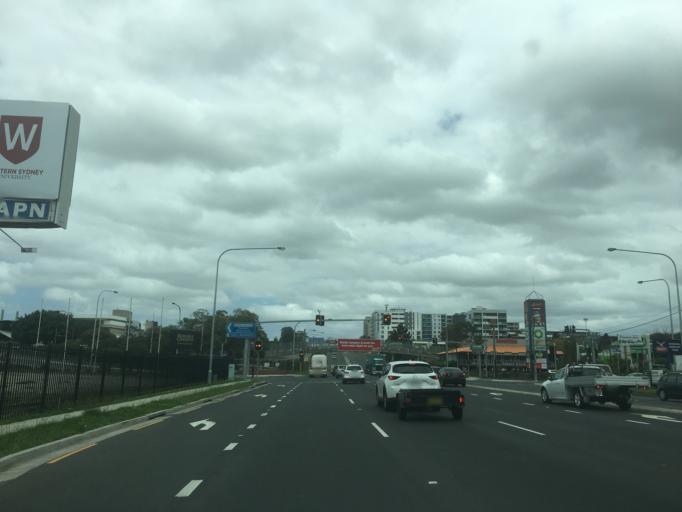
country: AU
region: New South Wales
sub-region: Parramatta
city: Harris Park
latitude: -33.8185
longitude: 151.0221
